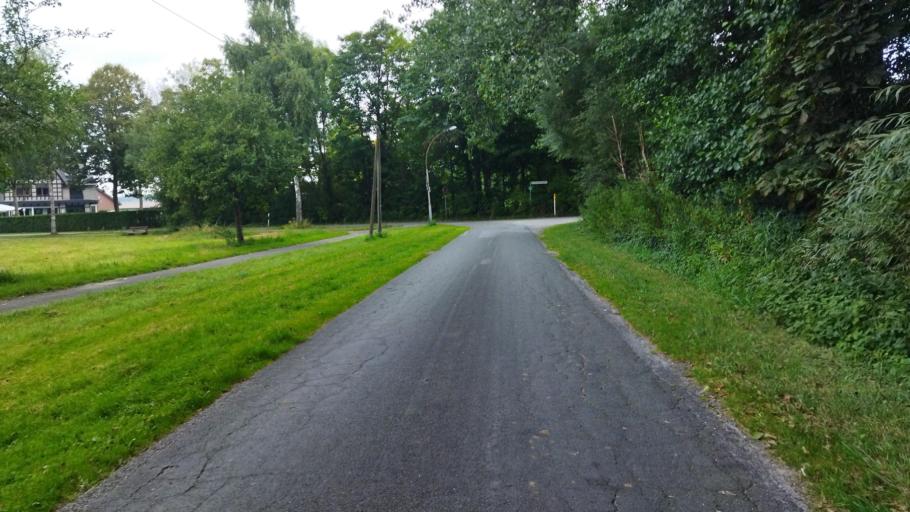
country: DE
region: Lower Saxony
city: Bad Laer
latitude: 52.0907
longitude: 8.0988
